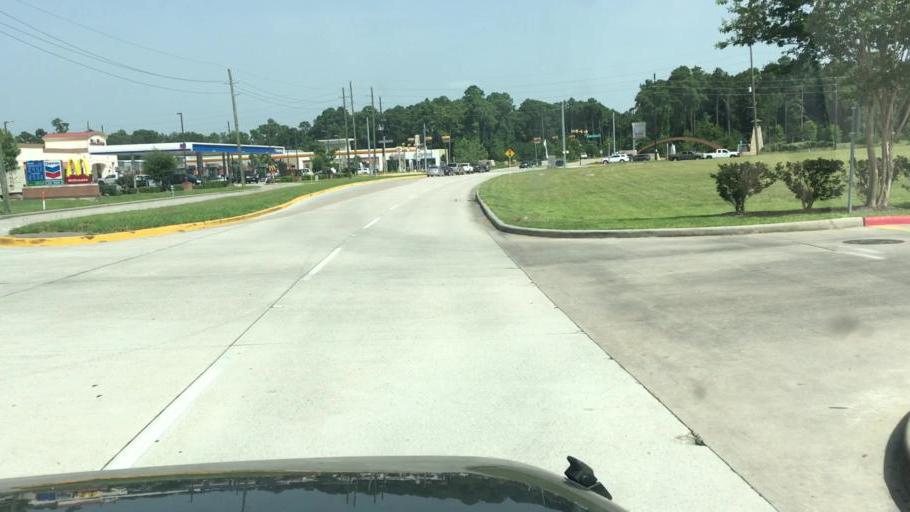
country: US
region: Texas
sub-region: Harris County
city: Atascocita
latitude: 29.9810
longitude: -95.1664
